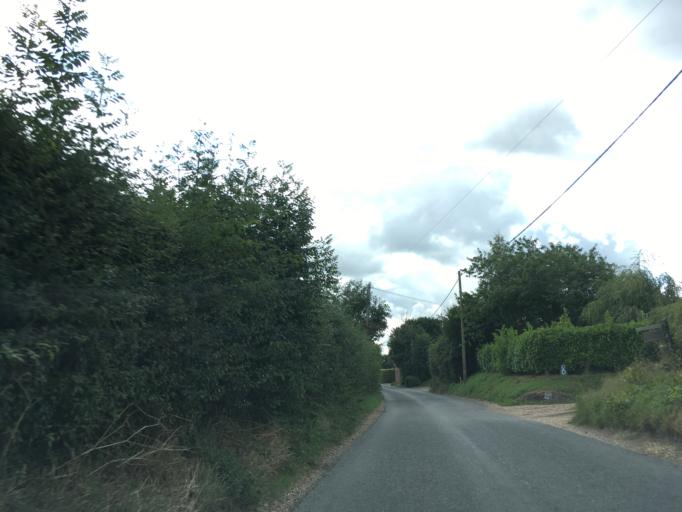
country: GB
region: England
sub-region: Hampshire
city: Overton
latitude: 51.2118
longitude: -1.3745
